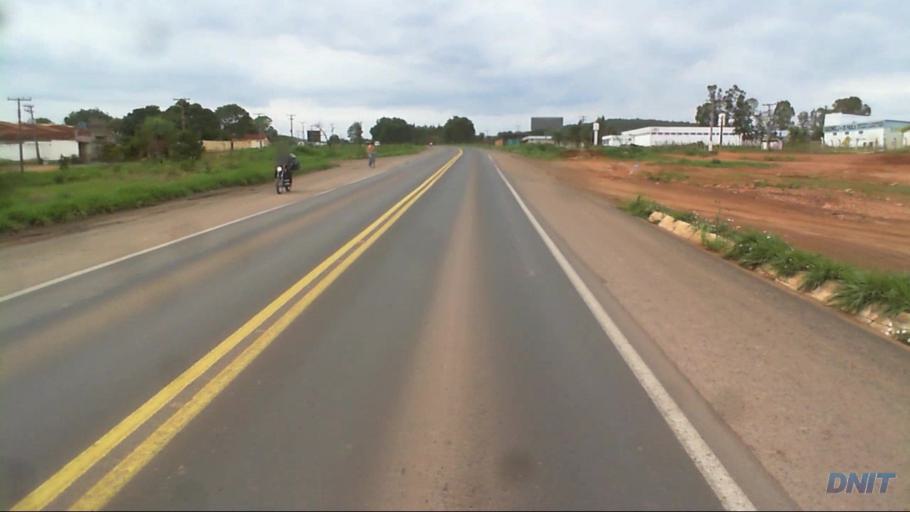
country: BR
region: Goias
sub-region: Uruacu
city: Uruacu
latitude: -14.5377
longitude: -49.1619
